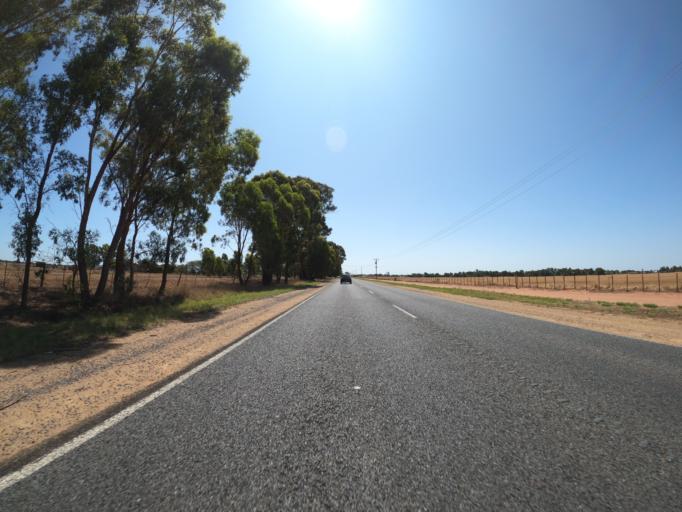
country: AU
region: Victoria
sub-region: Moira
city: Yarrawonga
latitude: -36.0204
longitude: 146.0556
